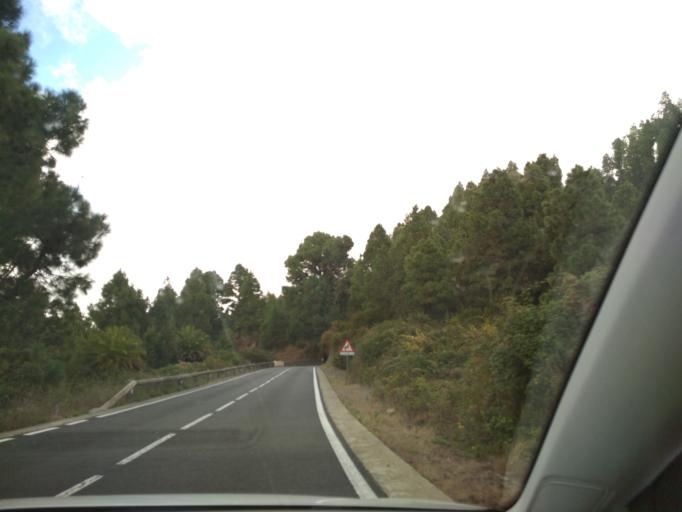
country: ES
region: Canary Islands
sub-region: Provincia de Santa Cruz de Tenerife
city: Garachico
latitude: 28.3372
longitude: -16.7569
